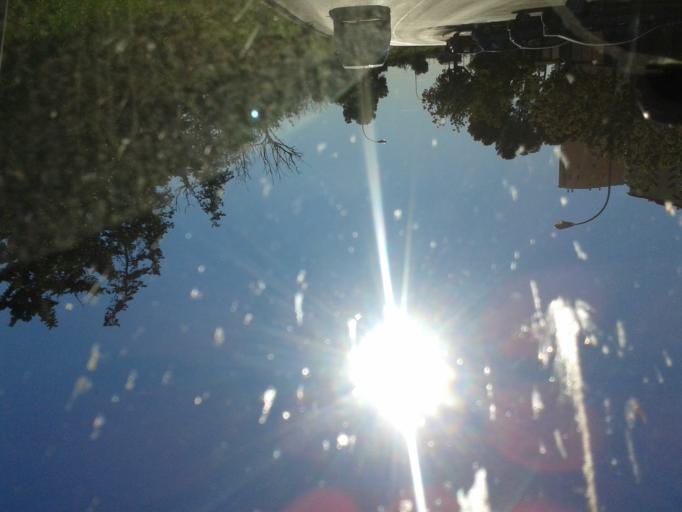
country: ES
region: Valencia
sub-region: Provincia de Alicante
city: el Campello
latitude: 38.4083
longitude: -0.4085
